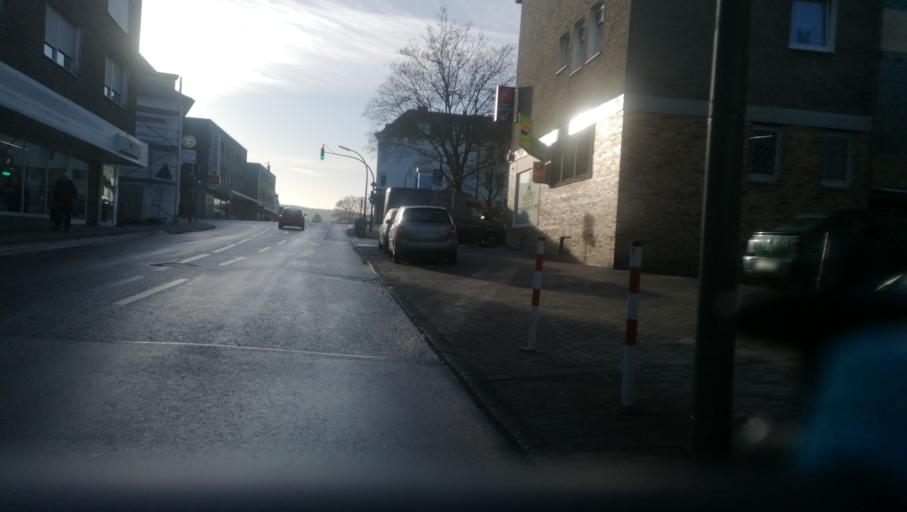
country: DE
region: North Rhine-Westphalia
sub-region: Regierungsbezirk Arnsberg
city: Dortmund
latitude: 51.4702
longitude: 7.4912
